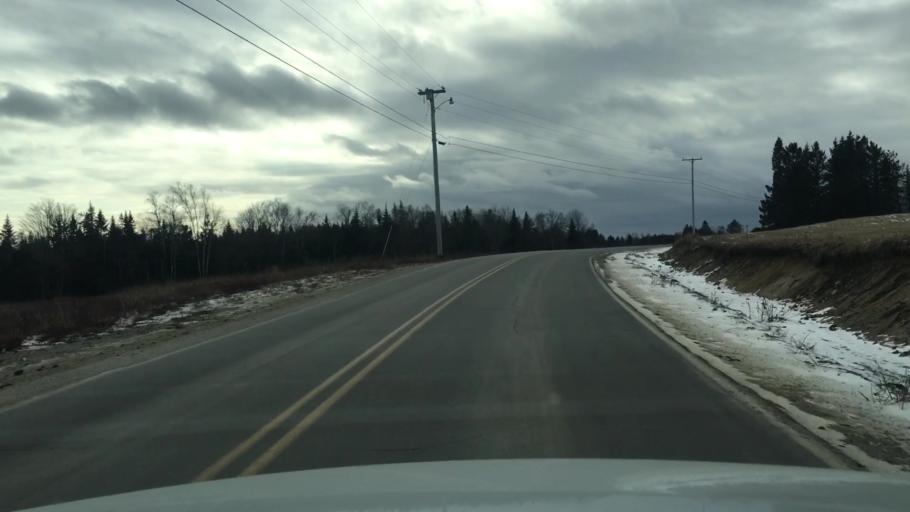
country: US
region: Maine
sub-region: Washington County
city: Jonesport
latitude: 44.6220
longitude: -67.6021
